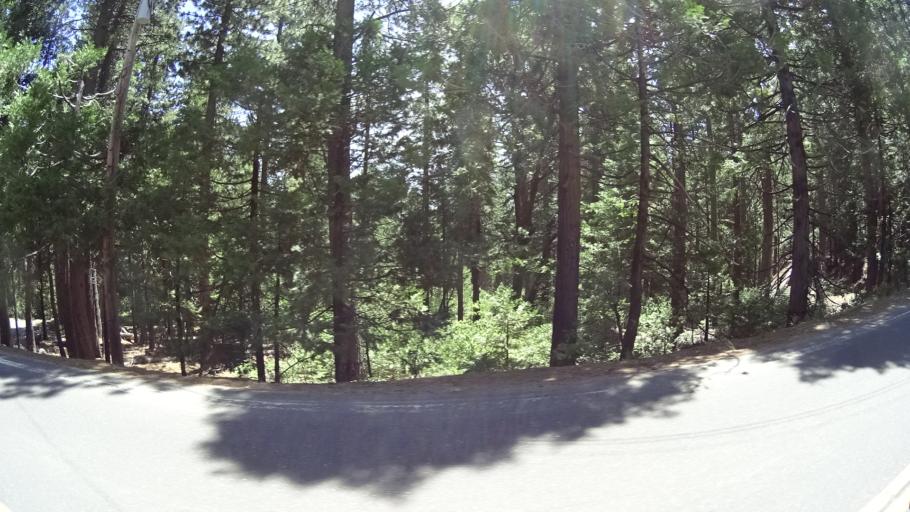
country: US
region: California
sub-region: Calaveras County
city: Arnold
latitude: 38.3208
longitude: -120.2519
